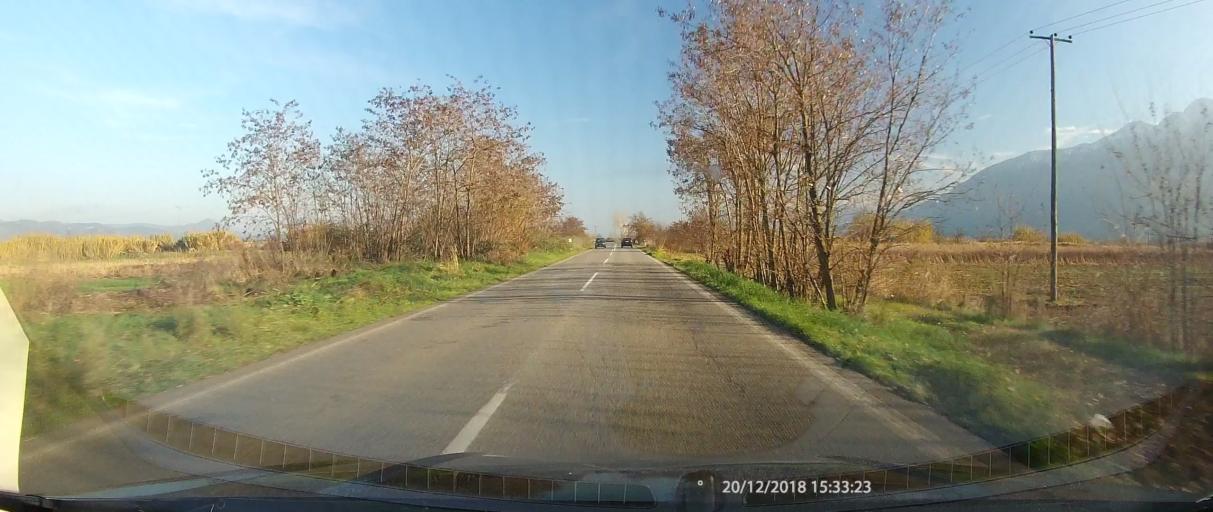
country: GR
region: Central Greece
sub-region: Nomos Fthiotidos
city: Lianokladhion
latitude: 38.9243
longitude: 22.2752
